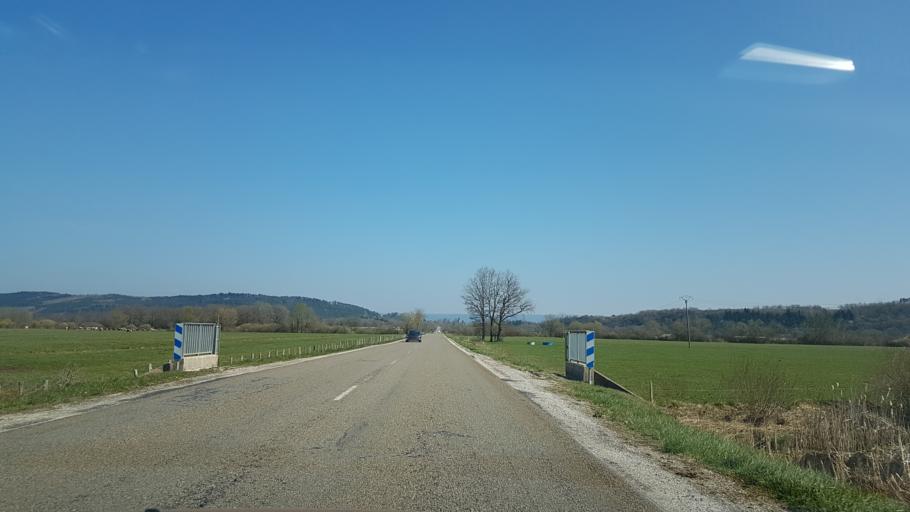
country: FR
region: Franche-Comte
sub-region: Departement du Jura
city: Orgelet
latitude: 46.5254
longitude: 5.5705
